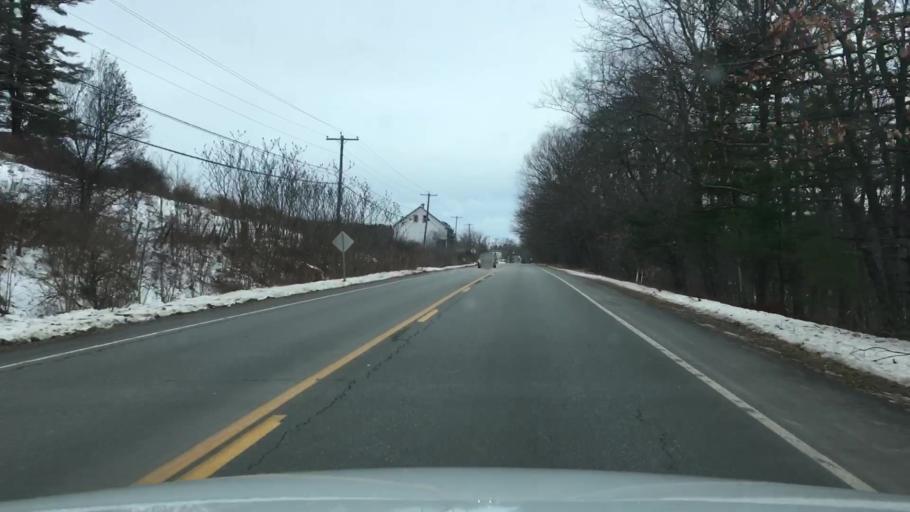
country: US
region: Maine
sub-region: Androscoggin County
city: Lewiston
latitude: 44.0661
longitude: -70.2088
